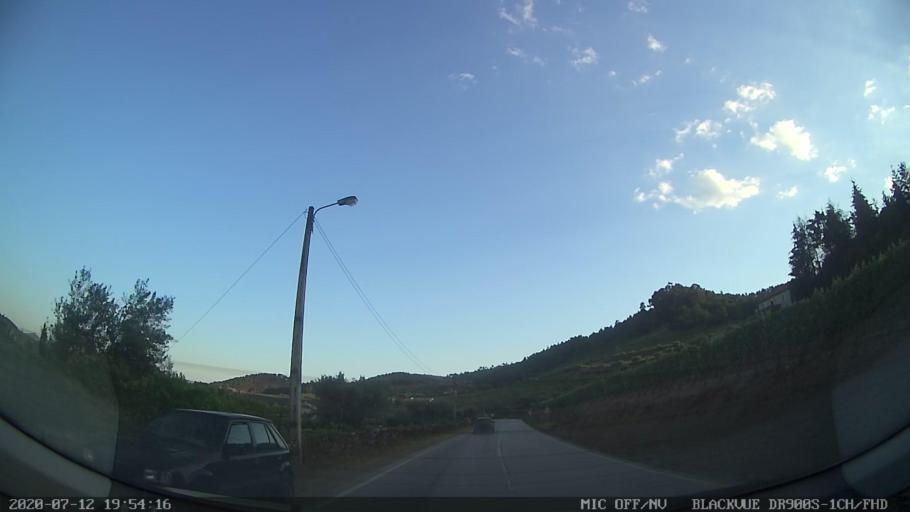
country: PT
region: Viseu
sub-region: Sao Joao da Pesqueira
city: Sao Joao da Pesqueira
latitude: 41.2579
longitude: -7.4406
